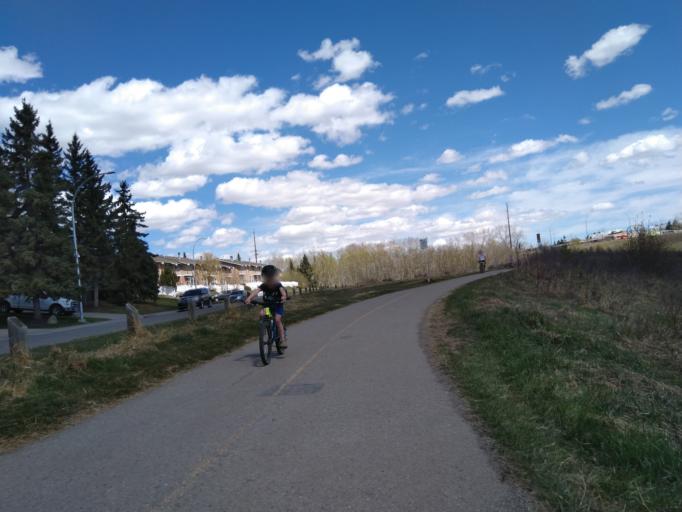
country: CA
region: Alberta
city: Calgary
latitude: 51.1016
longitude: -114.1924
